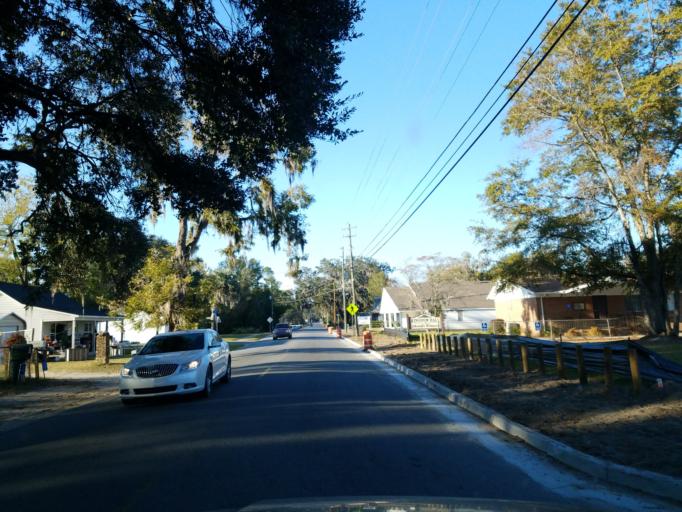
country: US
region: Georgia
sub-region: Lanier County
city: Lakeland
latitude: 31.0366
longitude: -83.0699
